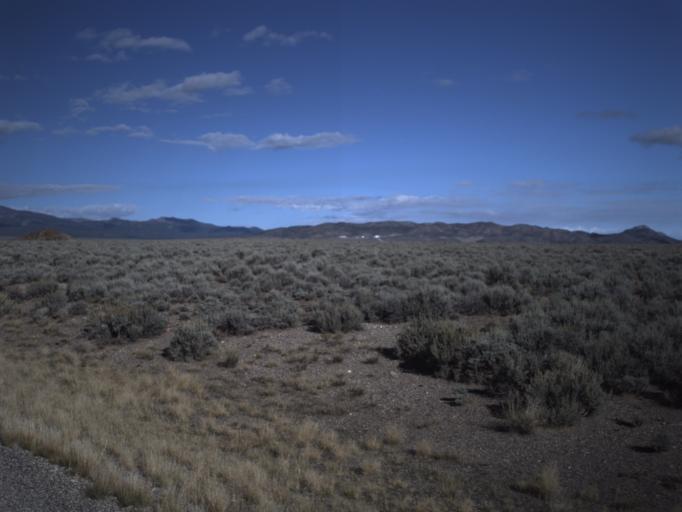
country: US
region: Utah
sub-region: Beaver County
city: Milford
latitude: 38.4150
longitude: -113.0795
